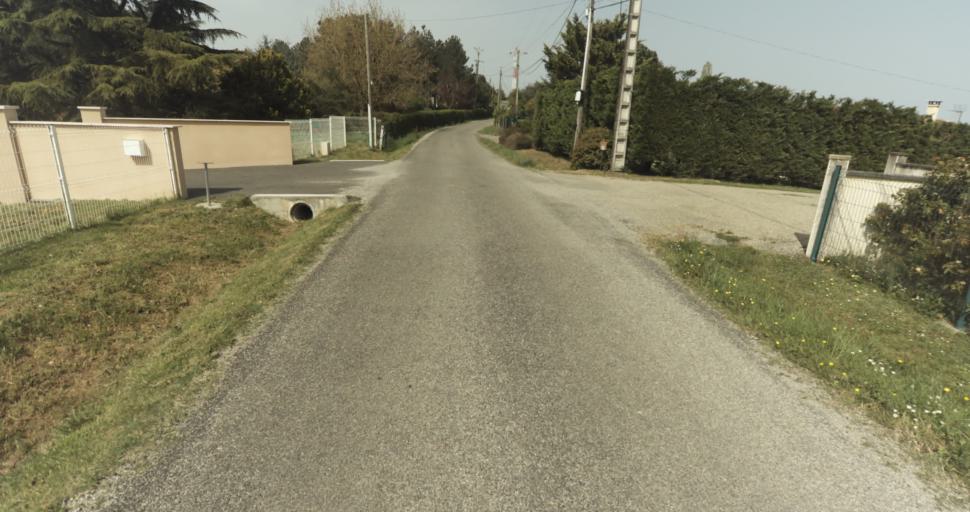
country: FR
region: Midi-Pyrenees
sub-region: Departement du Tarn-et-Garonne
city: Moissac
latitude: 44.1074
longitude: 1.0760
